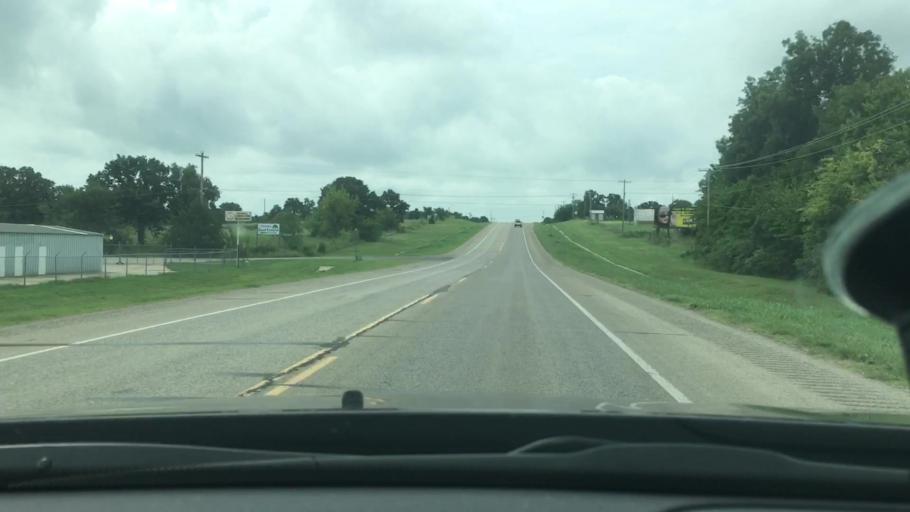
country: US
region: Oklahoma
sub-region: Carter County
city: Healdton
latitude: 34.2064
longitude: -97.4748
